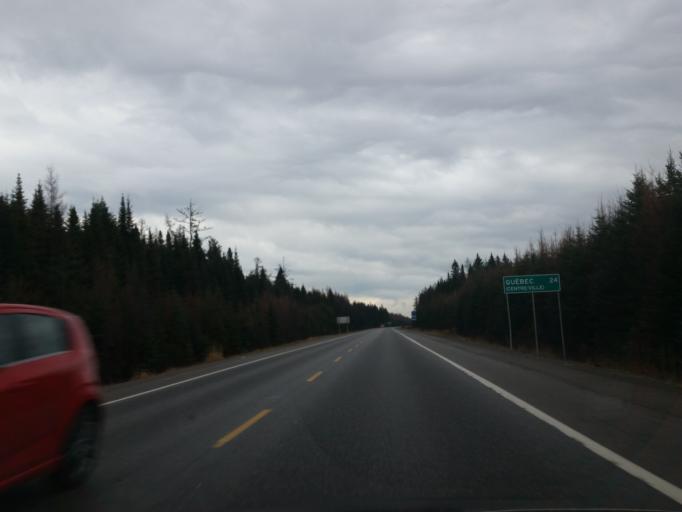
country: CA
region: Quebec
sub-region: Capitale-Nationale
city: Shannon
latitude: 46.8794
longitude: -71.4627
